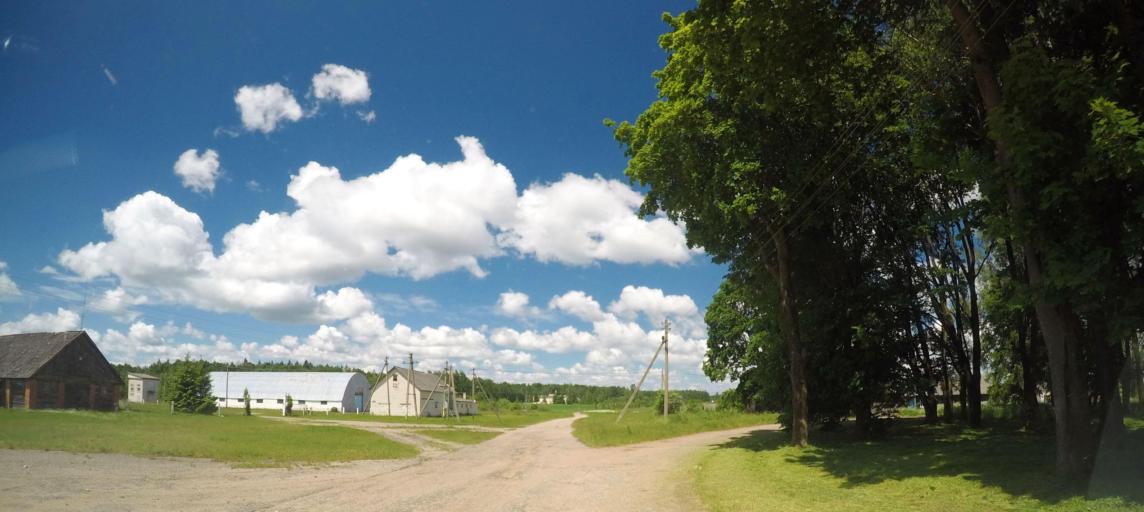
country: BY
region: Grodnenskaya
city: Hal'shany
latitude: 54.1642
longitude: 26.0868
